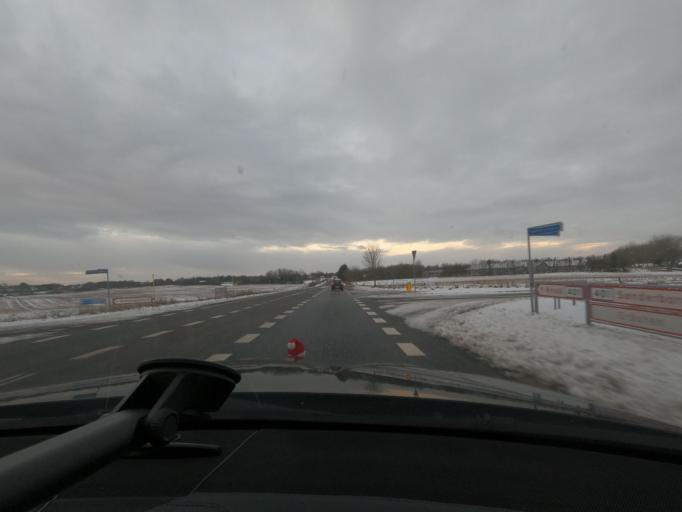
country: DK
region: South Denmark
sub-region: Aabenraa Kommune
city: Krusa
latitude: 54.8726
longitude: 9.4639
